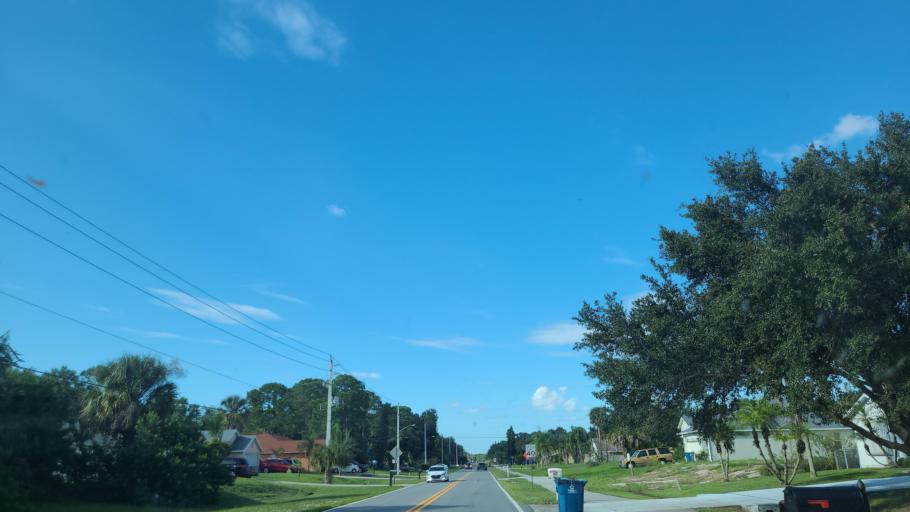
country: US
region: Florida
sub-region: Brevard County
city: Grant-Valkaria
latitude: 27.9609
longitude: -80.6610
